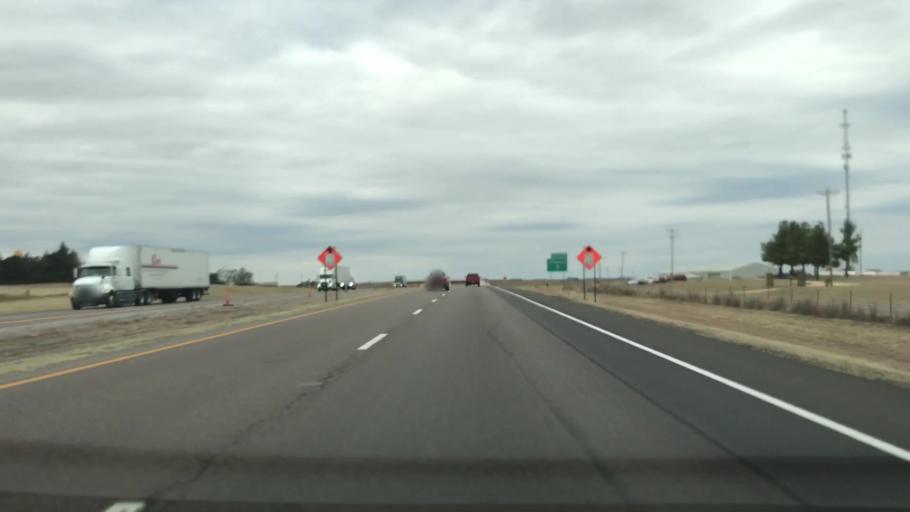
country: US
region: Oklahoma
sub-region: Washita County
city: Burns Flat
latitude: 35.4230
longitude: -99.2687
